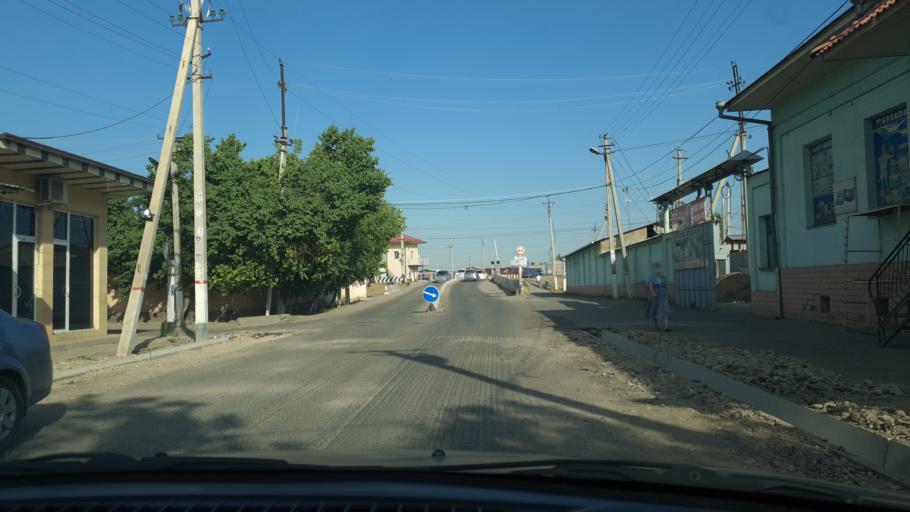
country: UZ
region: Toshkent
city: Urtaowul
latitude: 41.2007
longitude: 69.1567
